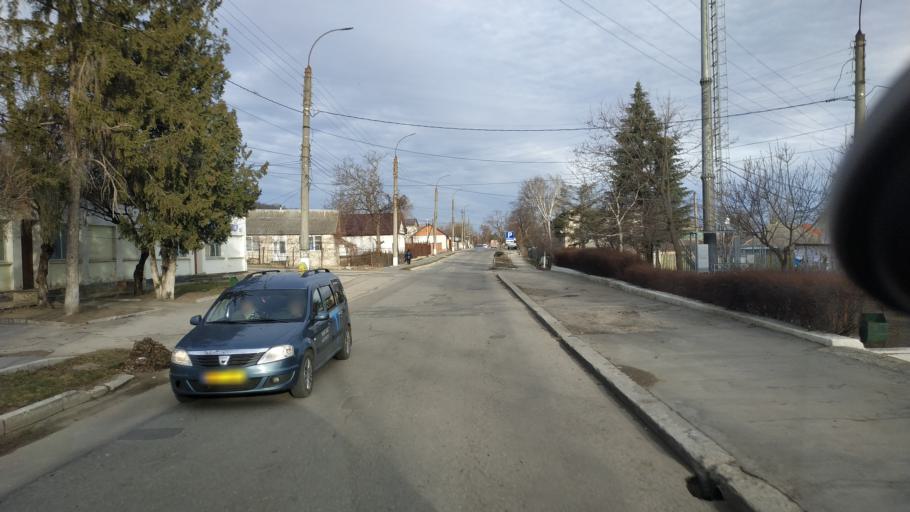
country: MD
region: Chisinau
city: Vadul lui Voda
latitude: 47.0917
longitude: 29.0759
